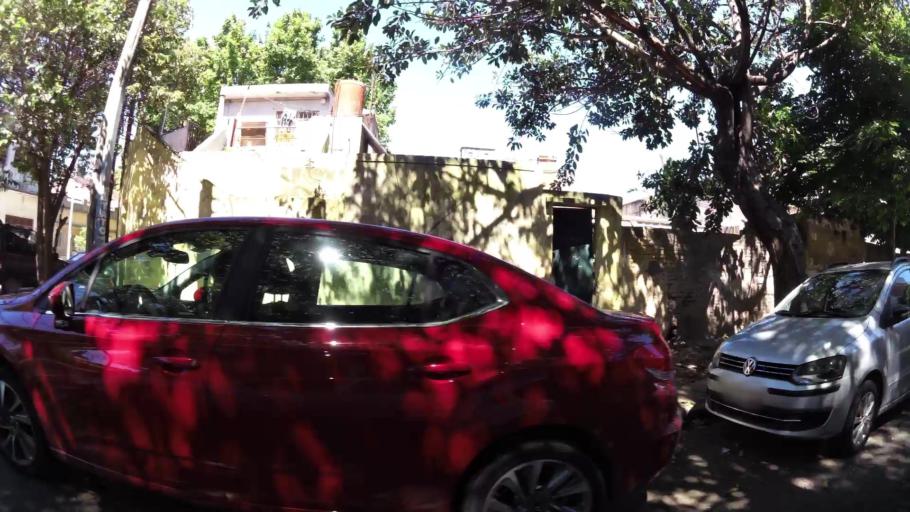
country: AR
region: Buenos Aires
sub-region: Partido de General San Martin
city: General San Martin
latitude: -34.5850
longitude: -58.5259
